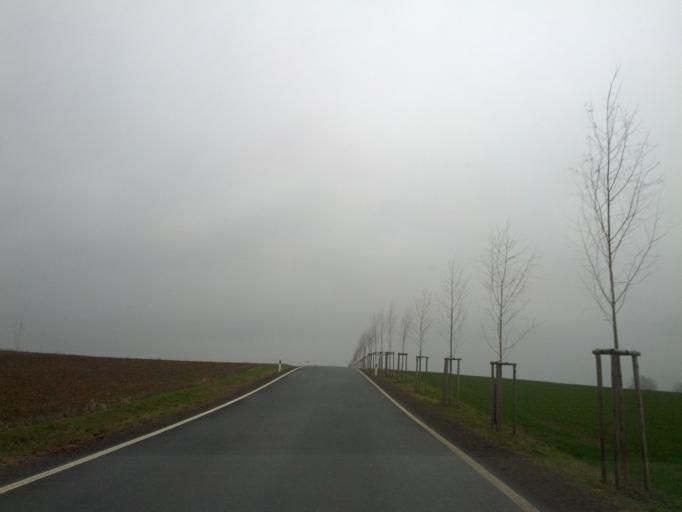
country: DE
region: Thuringia
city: Wangenheim
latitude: 51.0276
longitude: 10.6013
